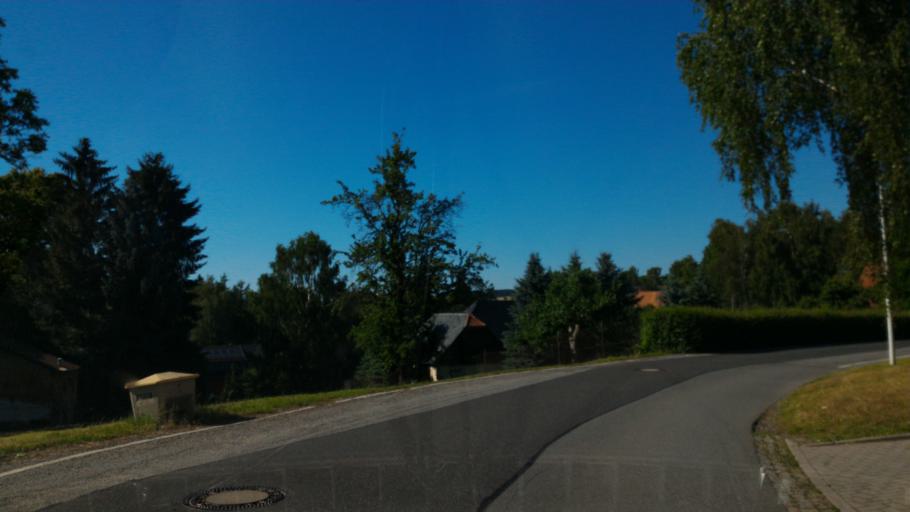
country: DE
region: Saxony
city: Mittelherwigsdorf
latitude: 50.9151
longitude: 14.7631
